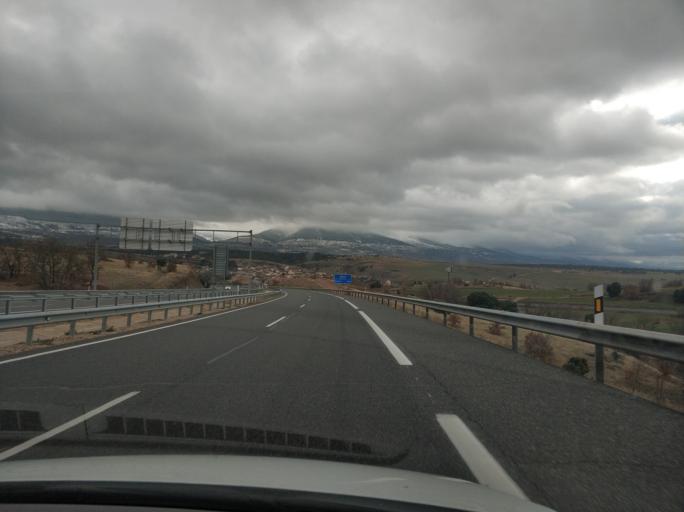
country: ES
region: Castille and Leon
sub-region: Provincia de Segovia
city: Cerezo de Abajo
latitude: 41.2291
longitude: -3.5913
